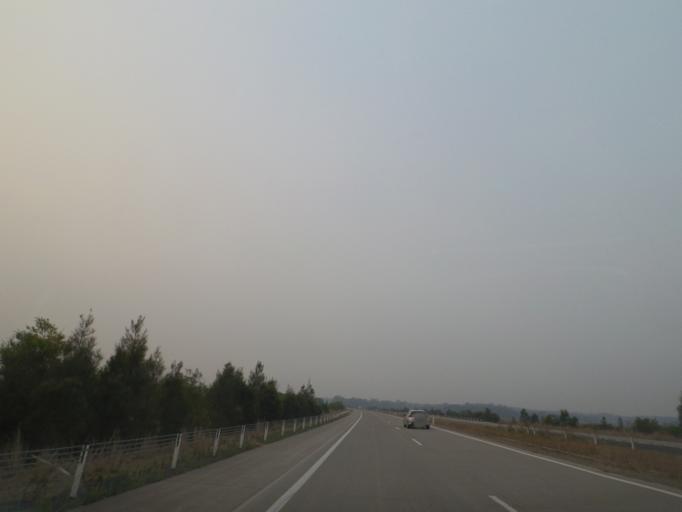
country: AU
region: New South Wales
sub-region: Kempsey
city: Frederickton
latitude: -30.9743
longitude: 152.8590
